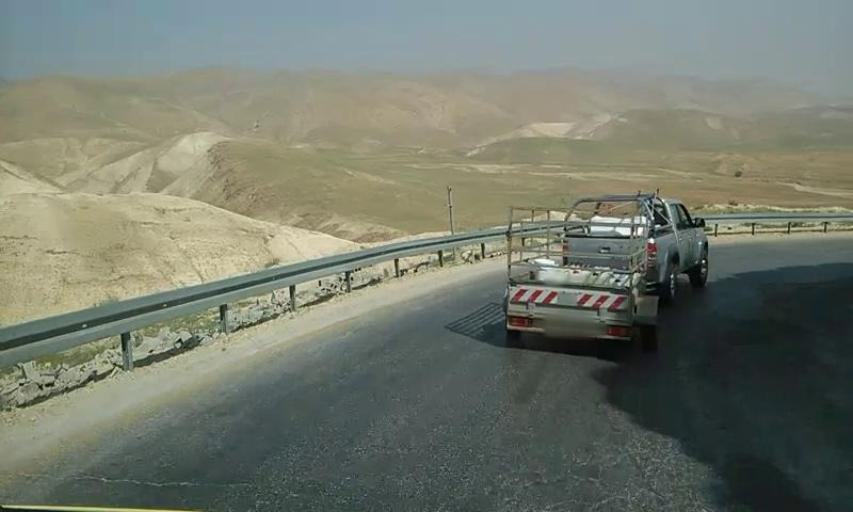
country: PS
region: West Bank
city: An Nuway`imah
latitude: 31.9177
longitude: 35.3874
